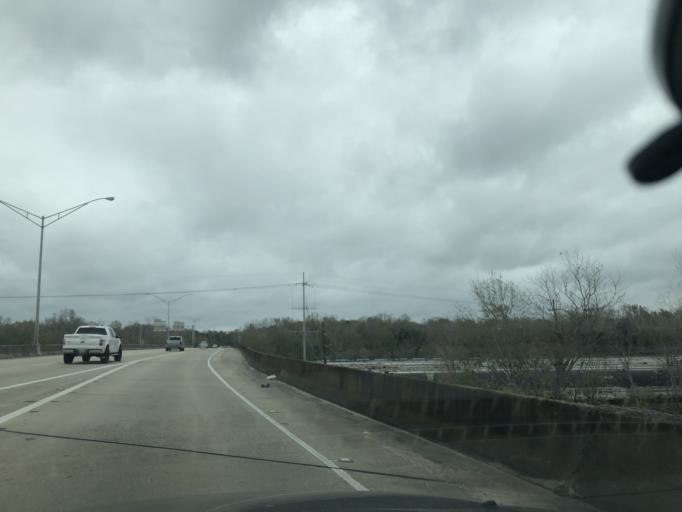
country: US
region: Louisiana
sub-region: Saint Charles Parish
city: Destrehan
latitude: 29.9530
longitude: -90.3676
